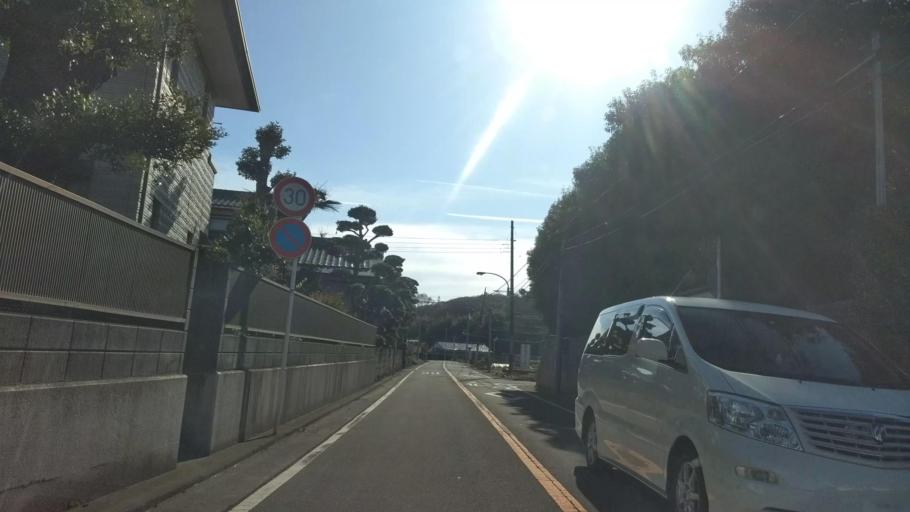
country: JP
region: Kanagawa
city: Hadano
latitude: 35.3362
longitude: 139.2327
